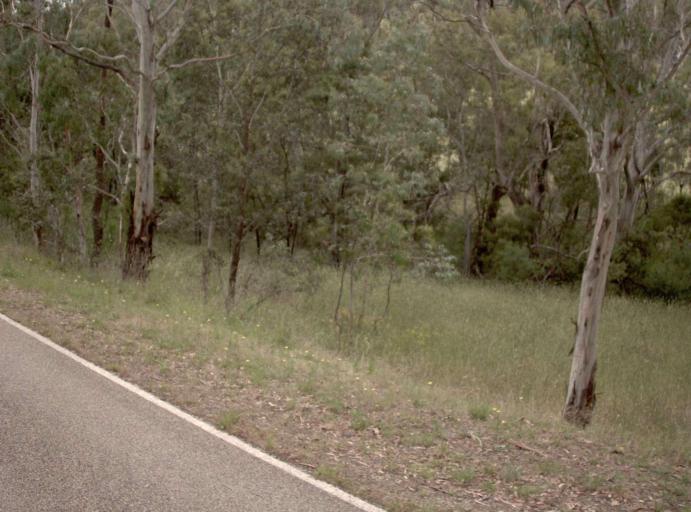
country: AU
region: Victoria
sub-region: East Gippsland
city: Bairnsdale
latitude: -37.5471
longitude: 147.2012
